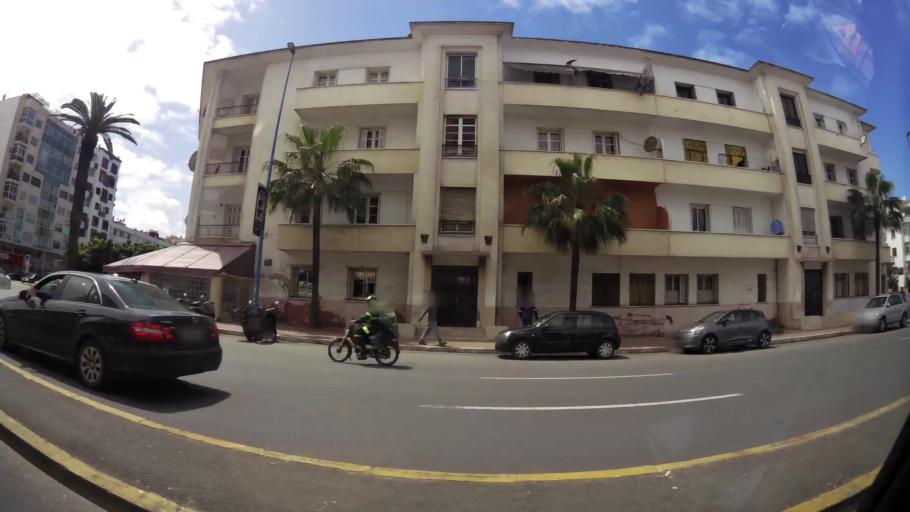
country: MA
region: Grand Casablanca
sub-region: Casablanca
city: Casablanca
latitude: 33.5944
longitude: -7.6379
